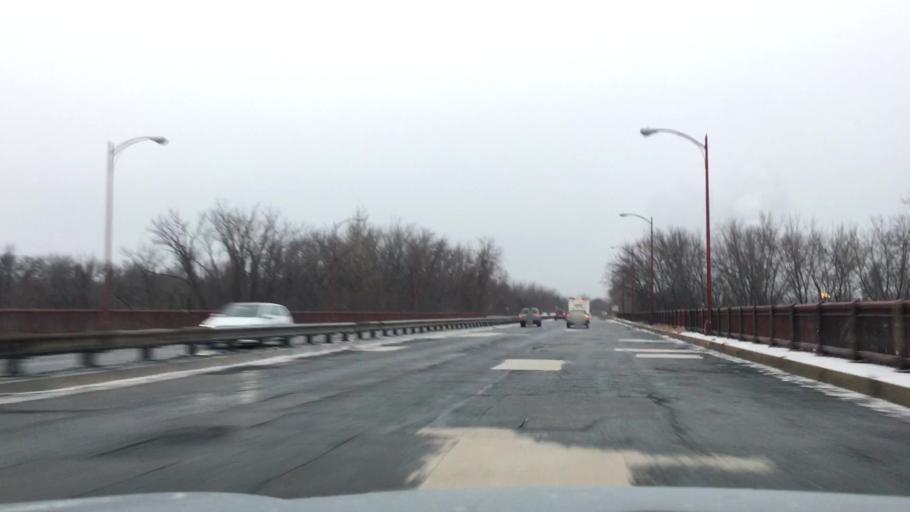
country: US
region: Massachusetts
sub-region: Hampden County
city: Springfield
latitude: 42.0831
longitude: -72.5915
